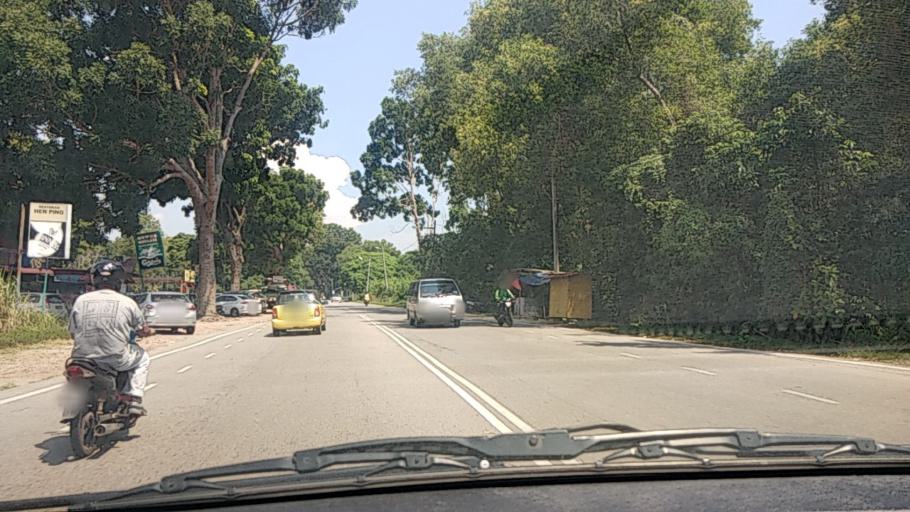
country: MY
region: Kedah
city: Sungai Petani
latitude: 5.6423
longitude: 100.5118
